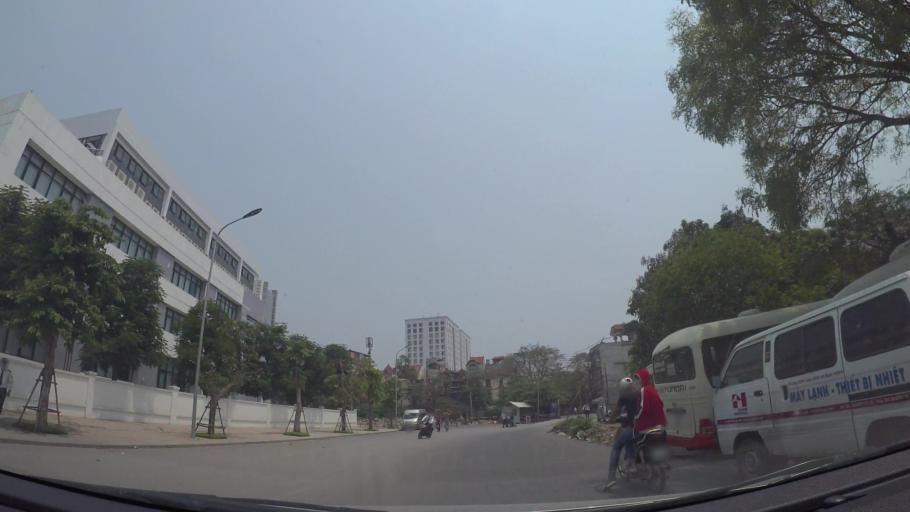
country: VN
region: Ha Noi
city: Thanh Xuan
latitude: 20.9980
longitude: 105.7870
